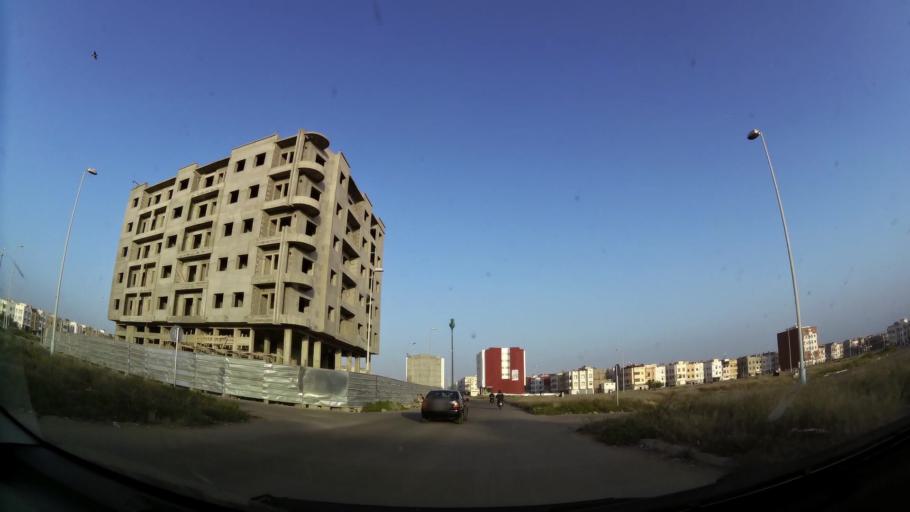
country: MA
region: Oued ed Dahab-Lagouira
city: Dakhla
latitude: 30.3998
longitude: -9.5653
